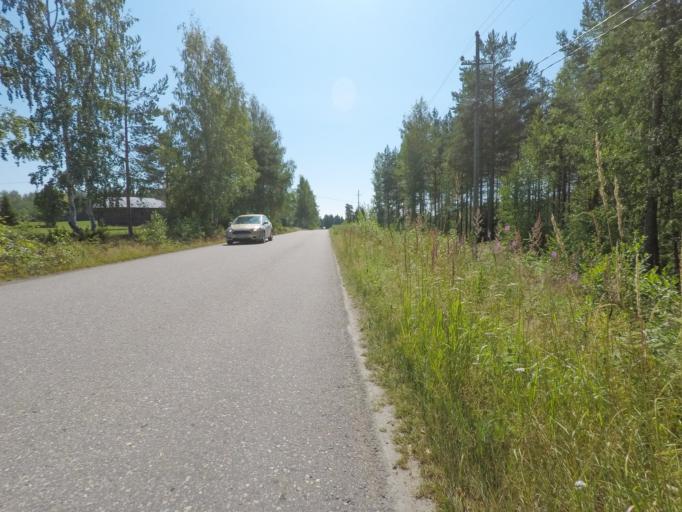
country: FI
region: Southern Savonia
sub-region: Mikkeli
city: Puumala
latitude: 61.4487
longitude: 28.1589
